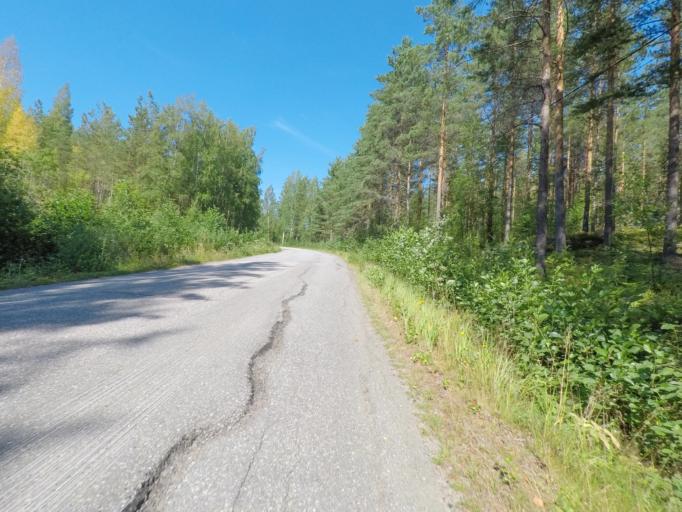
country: FI
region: Southern Savonia
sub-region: Mikkeli
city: Puumala
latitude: 61.4221
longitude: 28.1059
